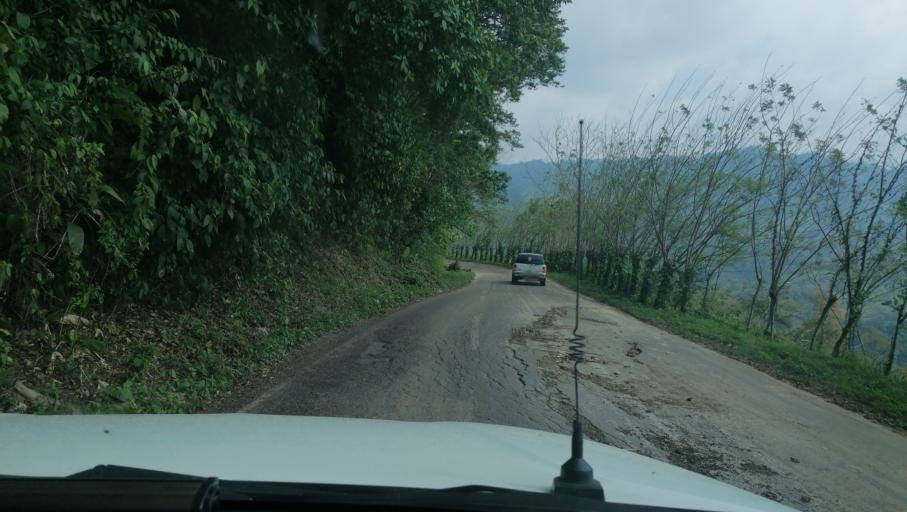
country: MX
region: Chiapas
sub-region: Francisco Leon
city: San Miguel la Sardina
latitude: 17.2285
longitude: -93.3492
